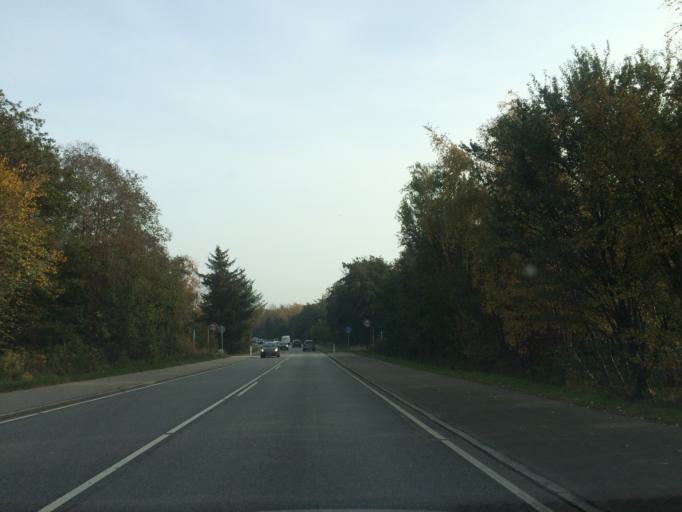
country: DK
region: Zealand
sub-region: Odsherred Kommune
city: Asnaes
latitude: 55.9791
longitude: 11.3229
